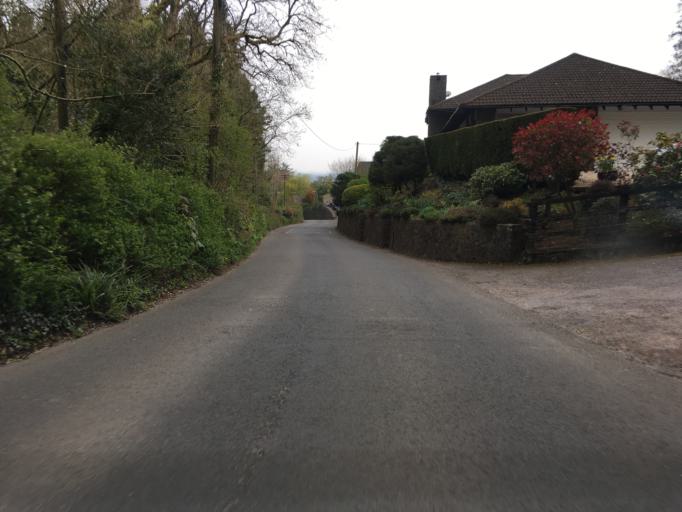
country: GB
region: Wales
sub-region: Cardiff
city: Radyr
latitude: 51.5355
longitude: -3.2302
